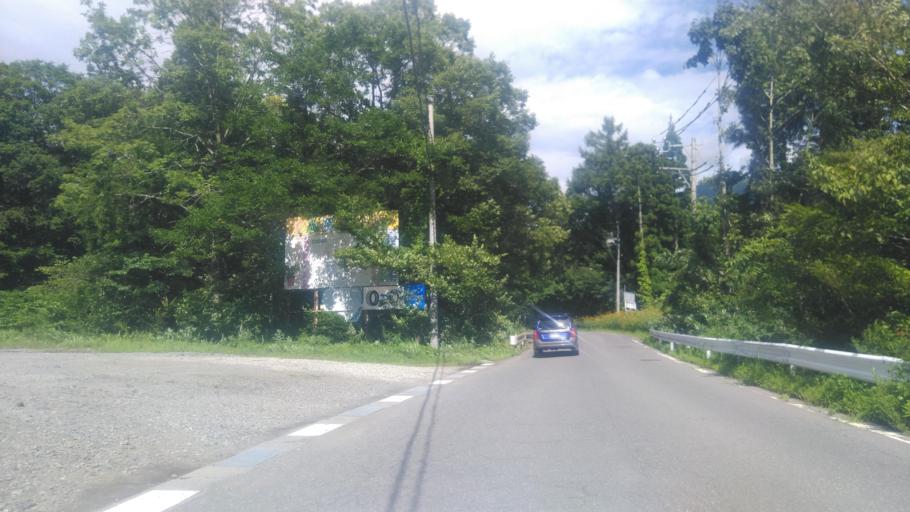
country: JP
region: Niigata
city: Arai
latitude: 36.8314
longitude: 138.1730
